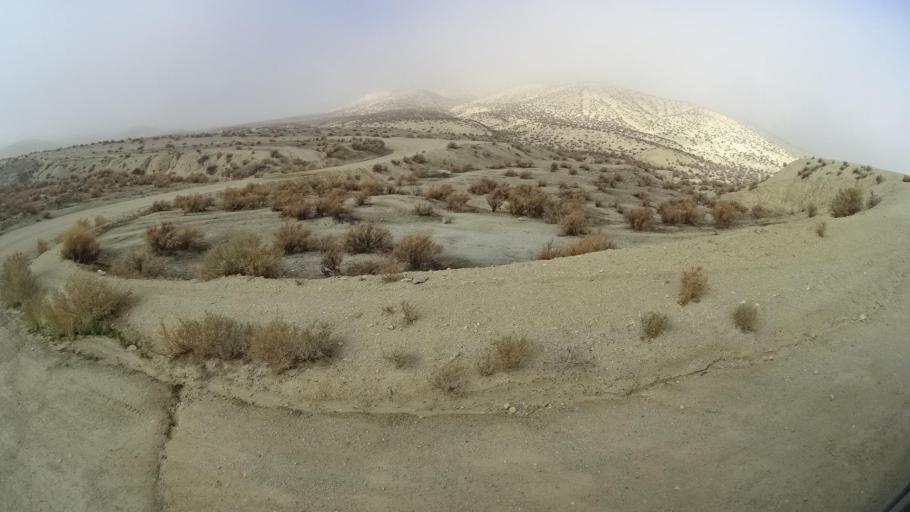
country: US
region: California
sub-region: Kern County
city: Maricopa
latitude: 35.0346
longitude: -119.4360
